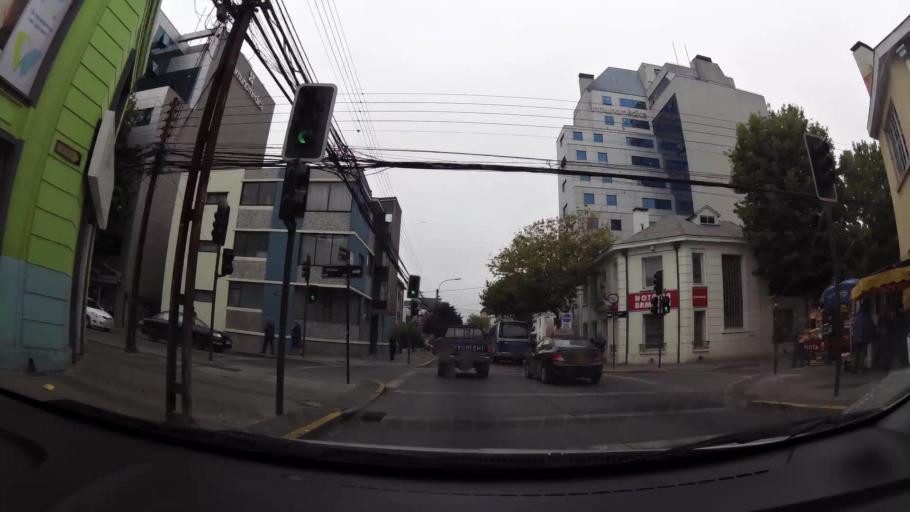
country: CL
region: Biobio
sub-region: Provincia de Concepcion
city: Concepcion
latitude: -36.8273
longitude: -73.0463
